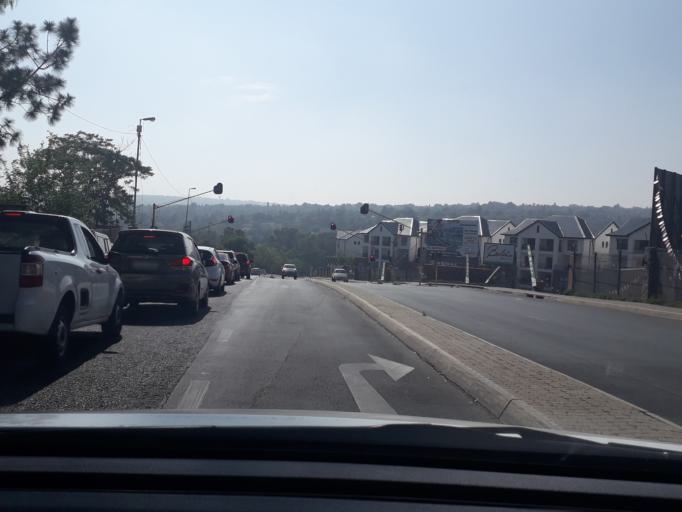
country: ZA
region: Gauteng
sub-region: City of Johannesburg Metropolitan Municipality
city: Diepsloot
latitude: -26.0592
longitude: 27.9770
